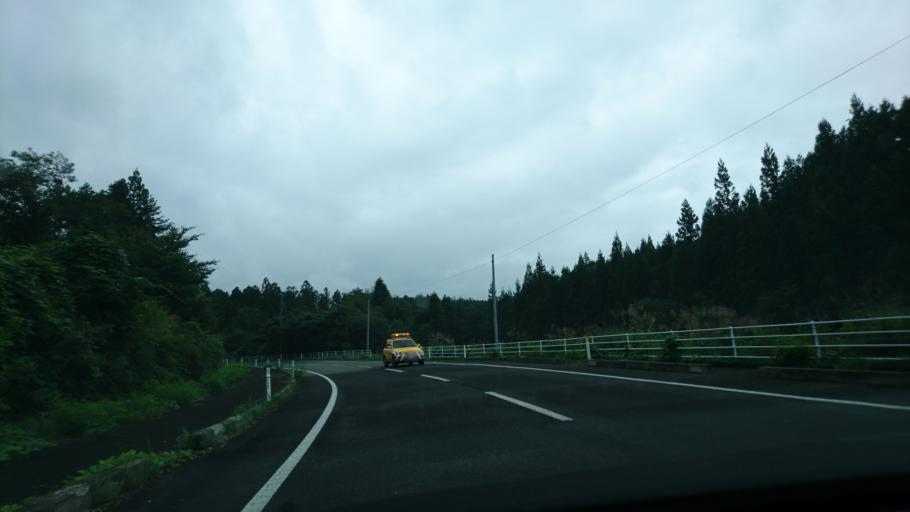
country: JP
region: Iwate
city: Ichinoseki
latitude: 38.8889
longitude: 140.9608
